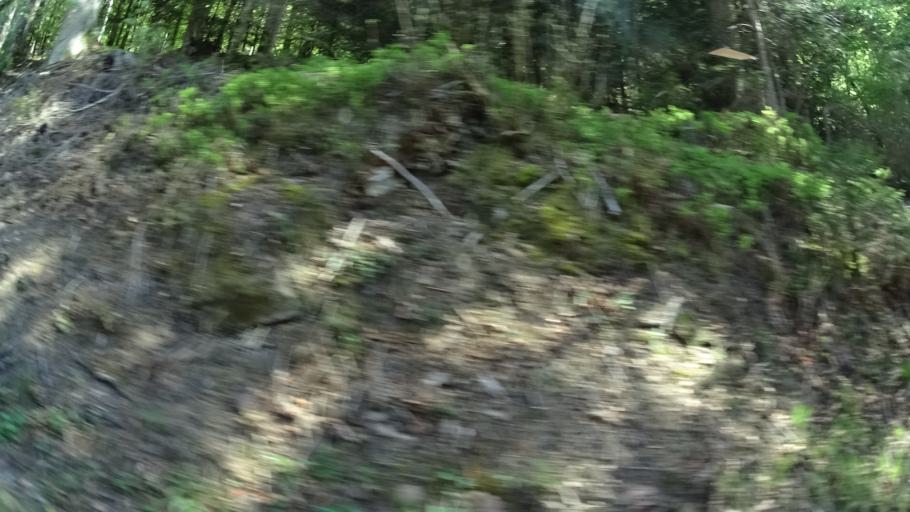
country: DE
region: Baden-Wuerttemberg
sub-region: Karlsruhe Region
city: Dobel
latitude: 48.7842
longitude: 8.5204
